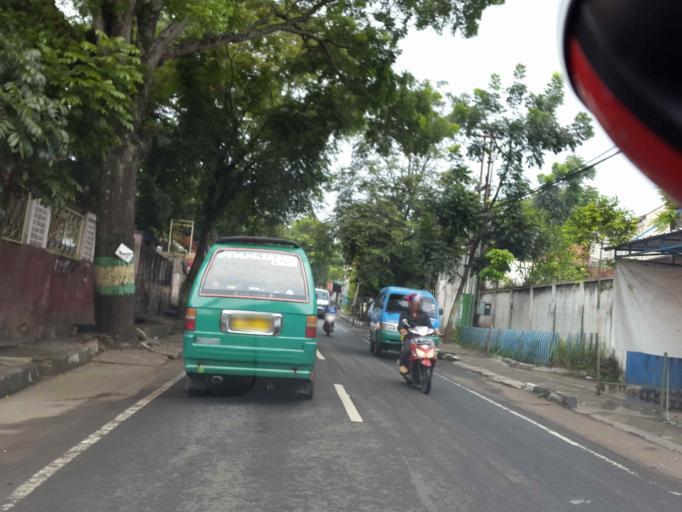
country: ID
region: West Java
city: Cimahi
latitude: -6.8609
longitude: 107.5477
